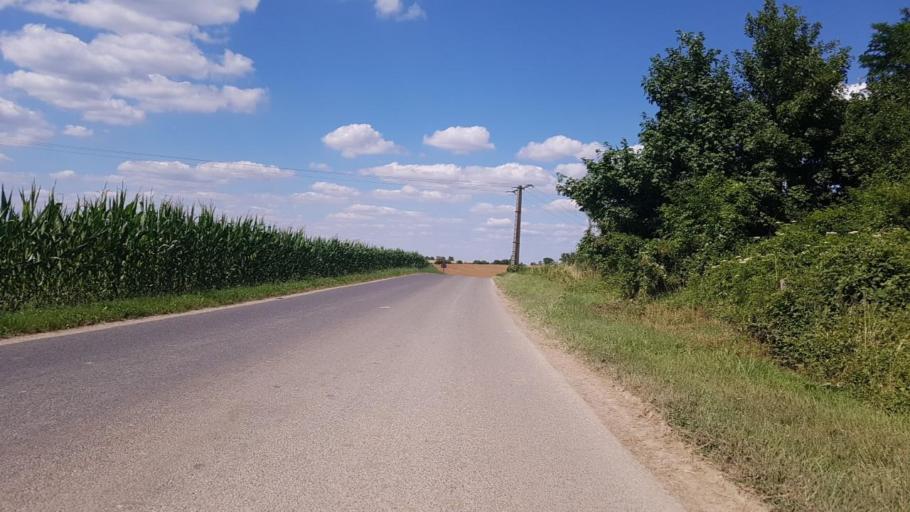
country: FR
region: Ile-de-France
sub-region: Departement de Seine-et-Marne
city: Moussy-le-Vieux
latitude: 49.0697
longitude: 2.6422
